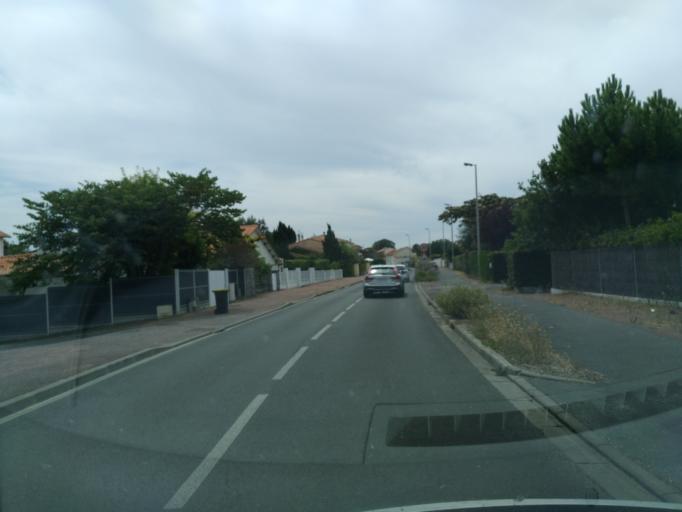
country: FR
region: Poitou-Charentes
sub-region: Departement de la Charente-Maritime
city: Saint-Palais-sur-Mer
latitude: 45.6480
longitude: -1.0824
